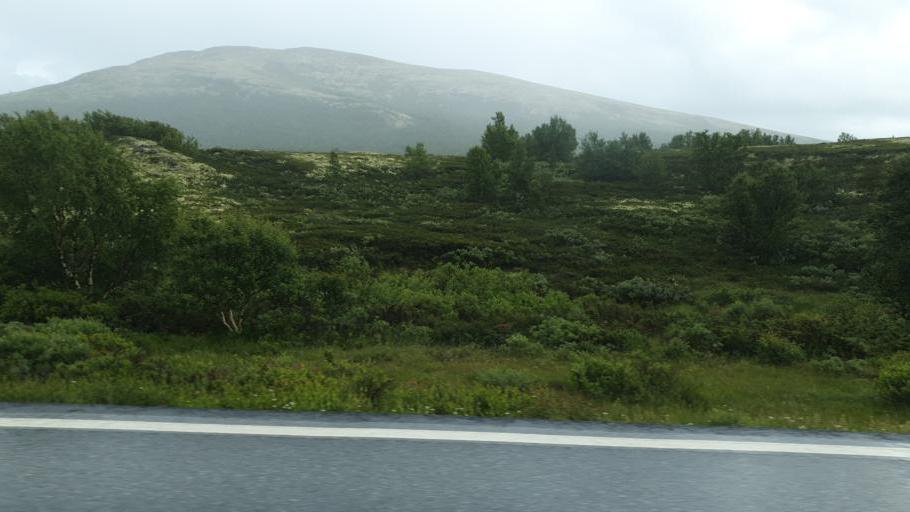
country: NO
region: Sor-Trondelag
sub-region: Oppdal
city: Oppdal
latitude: 62.2558
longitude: 9.5482
